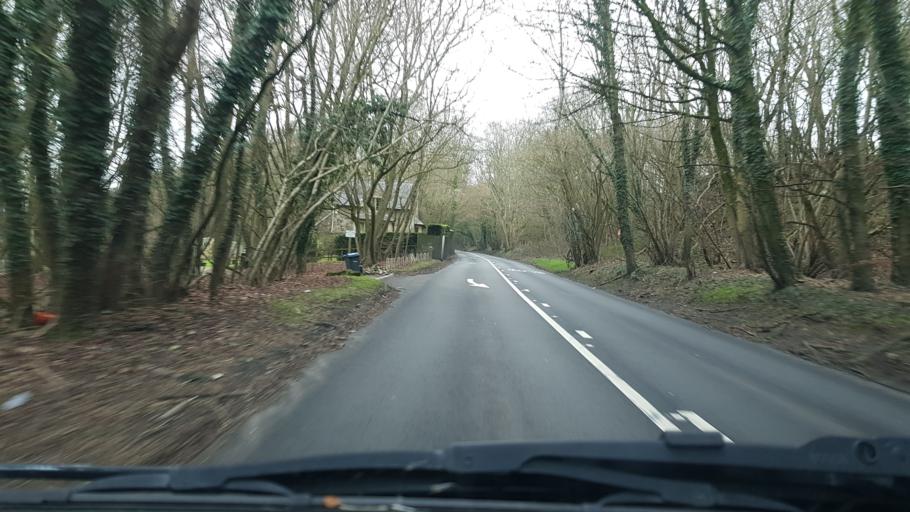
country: GB
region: England
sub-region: Wiltshire
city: Burbage
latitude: 51.3747
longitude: -1.6818
